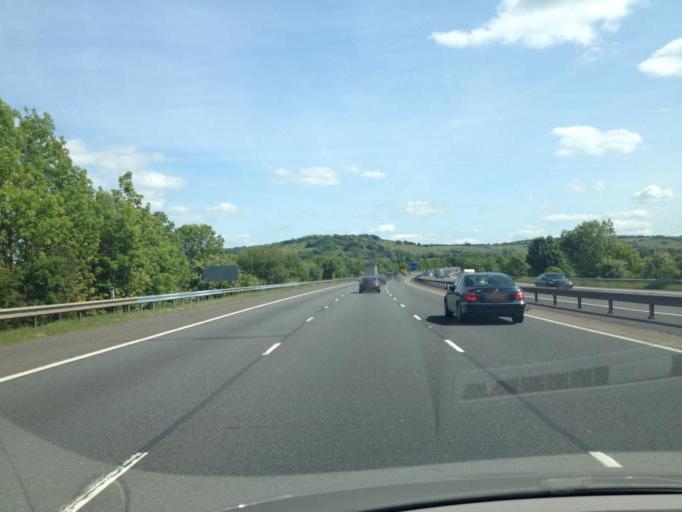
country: GB
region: England
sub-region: Oxfordshire
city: Watlington
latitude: 51.6797
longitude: -0.9675
